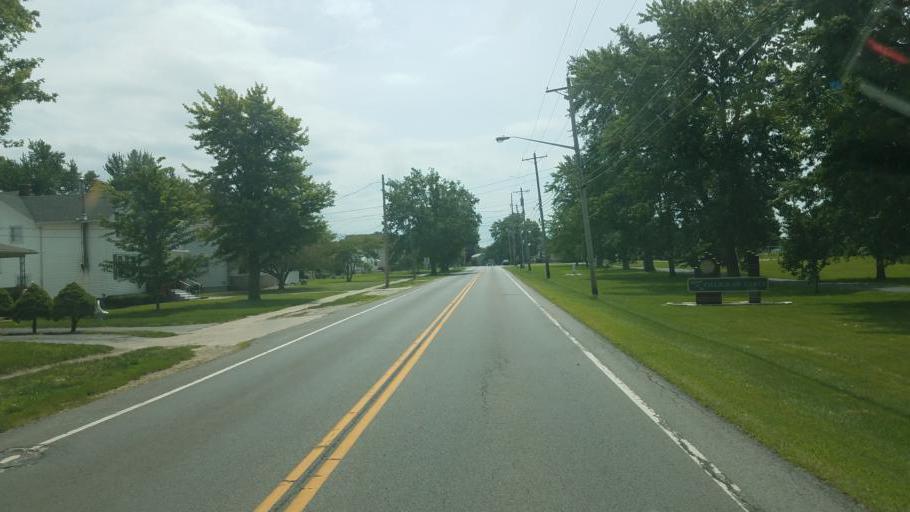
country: US
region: Ohio
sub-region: Wyandot County
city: Carey
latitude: 40.9556
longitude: -83.3958
